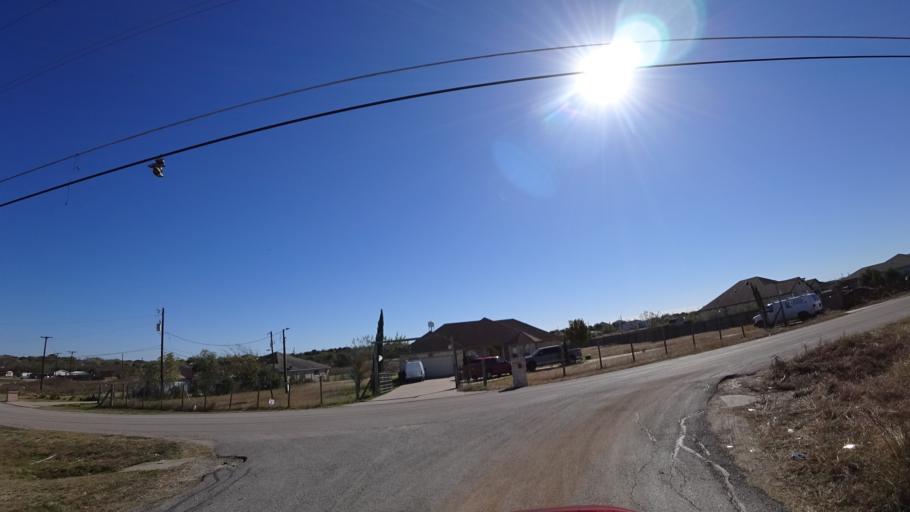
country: US
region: Texas
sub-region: Travis County
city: Garfield
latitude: 30.1038
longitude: -97.6036
